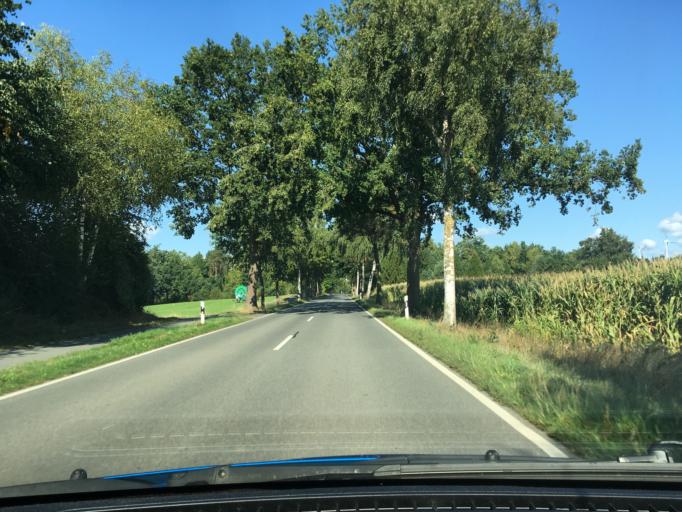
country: DE
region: Lower Saxony
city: Hermannsburg
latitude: 52.8560
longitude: 10.0566
